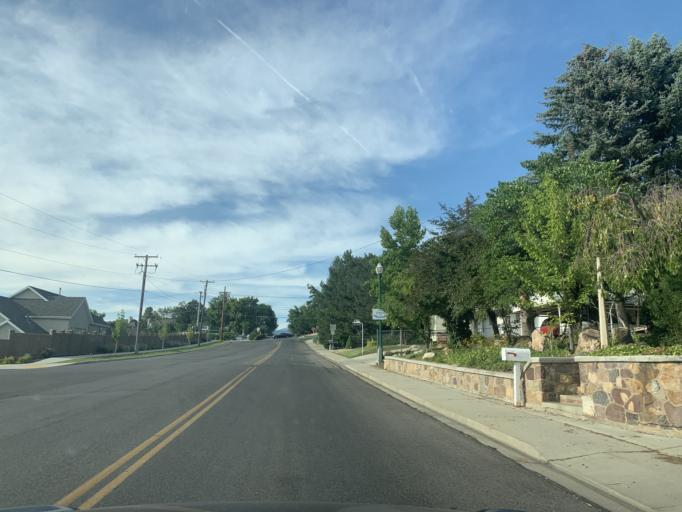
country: US
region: Utah
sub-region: Utah County
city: Orem
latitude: 40.2595
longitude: -111.6948
